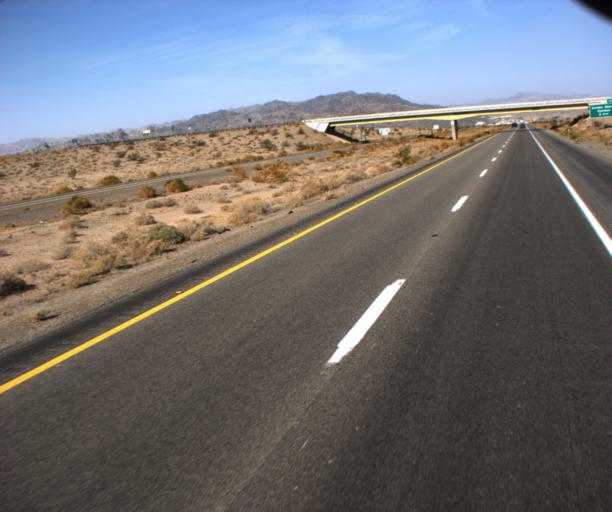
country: US
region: Arizona
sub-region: Mohave County
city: Desert Hills
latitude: 34.7225
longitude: -114.4337
